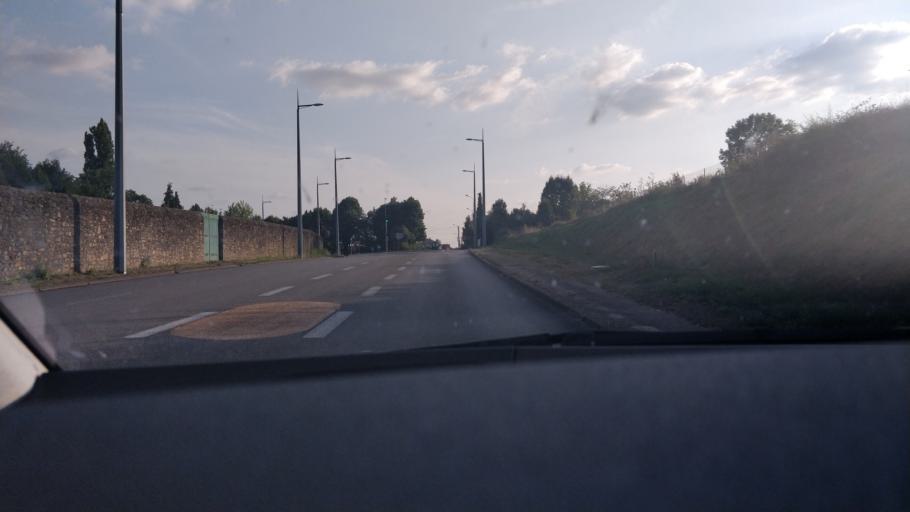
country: FR
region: Limousin
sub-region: Departement de la Haute-Vienne
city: Limoges
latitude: 45.8434
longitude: 1.2886
